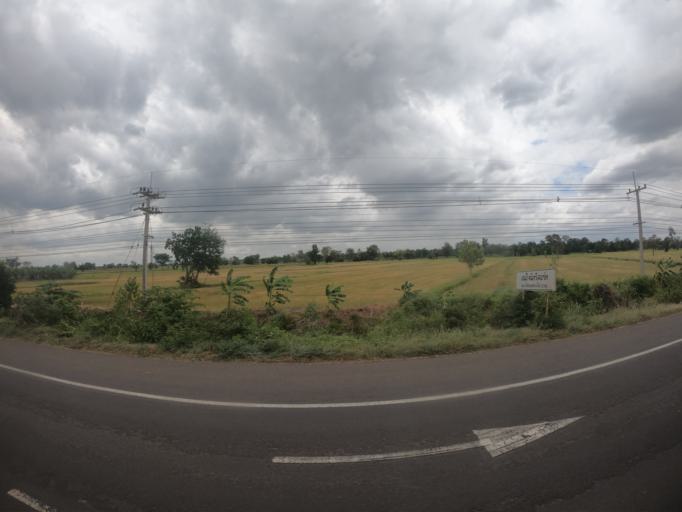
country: TH
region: Buriram
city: Nong Ki
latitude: 14.6935
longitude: 102.5097
